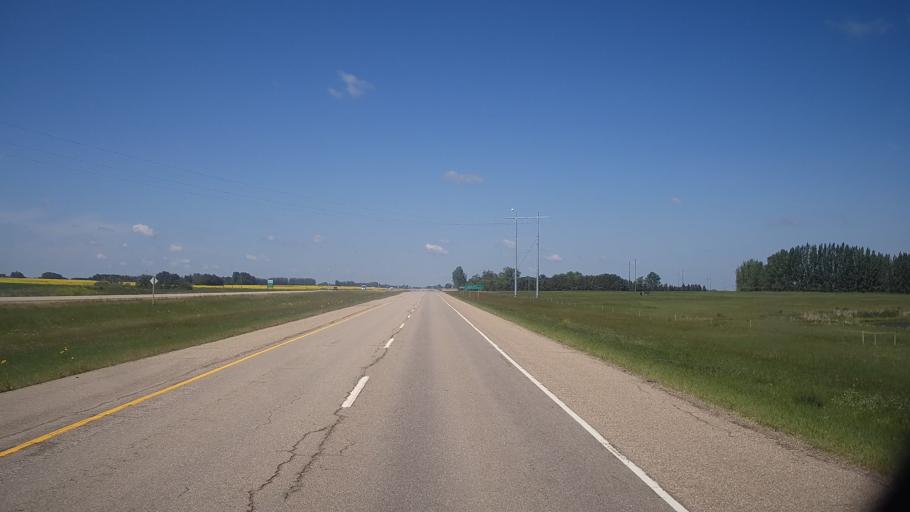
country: CA
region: Saskatchewan
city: Saskatoon
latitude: 51.9981
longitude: -106.3070
